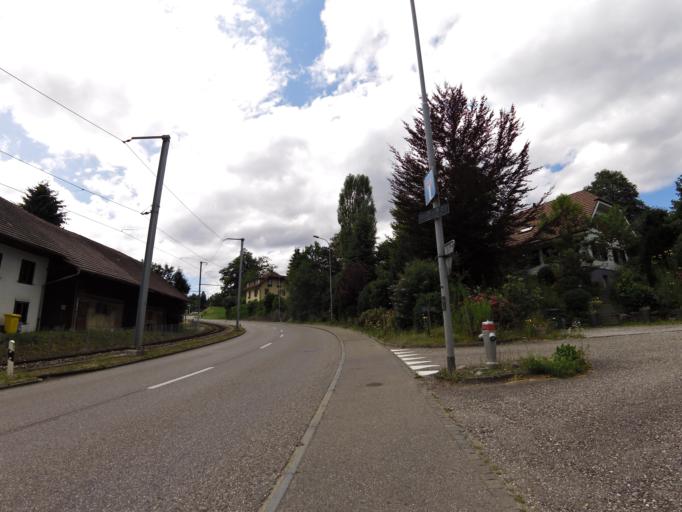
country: CH
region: Bern
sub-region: Oberaargau
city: Aarwangen
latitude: 47.2477
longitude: 7.7600
